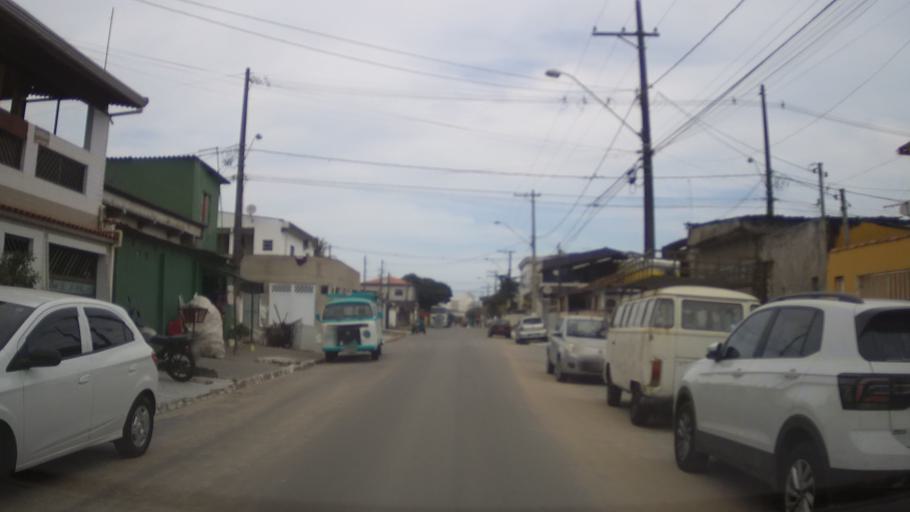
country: BR
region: Sao Paulo
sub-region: Praia Grande
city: Praia Grande
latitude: -24.0067
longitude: -46.4605
